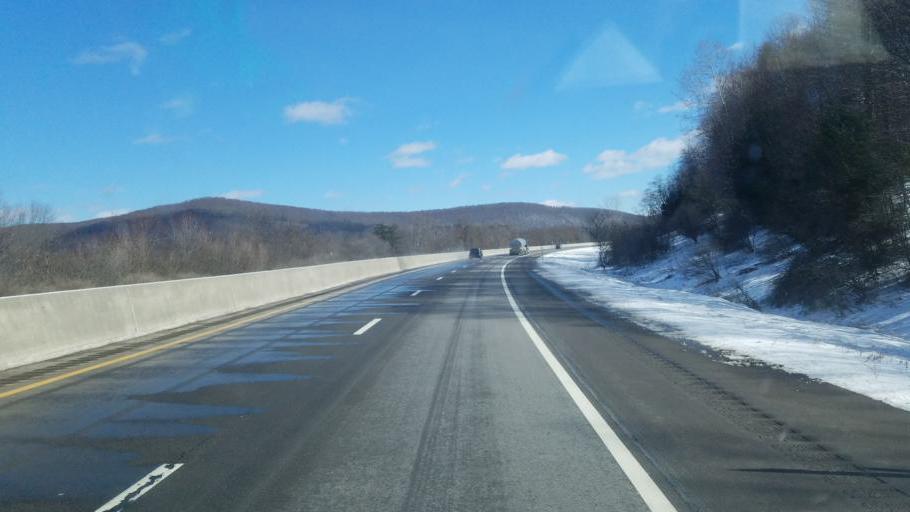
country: US
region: New York
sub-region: Cattaraugus County
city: Salamanca
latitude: 42.1466
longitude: -78.6725
